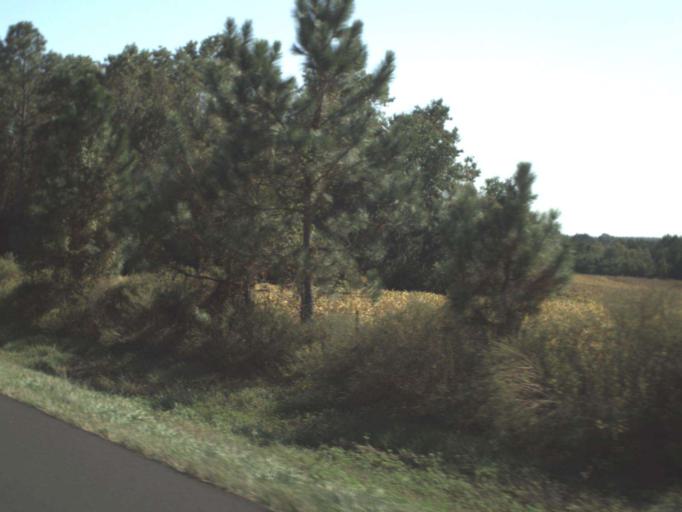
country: US
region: Alabama
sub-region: Covington County
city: Florala
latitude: 30.8857
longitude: -86.2764
